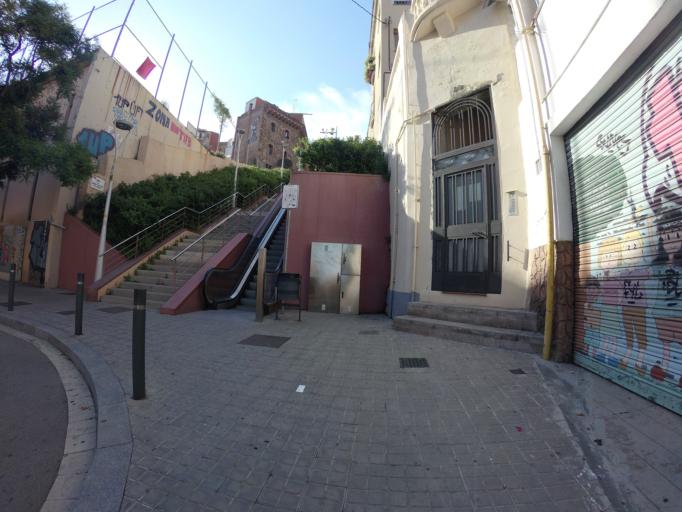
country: ES
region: Catalonia
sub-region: Provincia de Barcelona
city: Gracia
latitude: 41.4110
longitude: 2.1537
